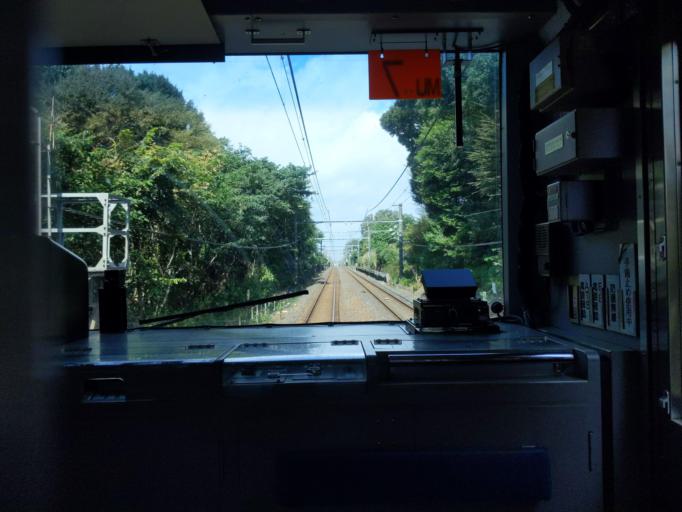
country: JP
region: Chiba
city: Matsudo
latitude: 35.7743
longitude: 139.9427
